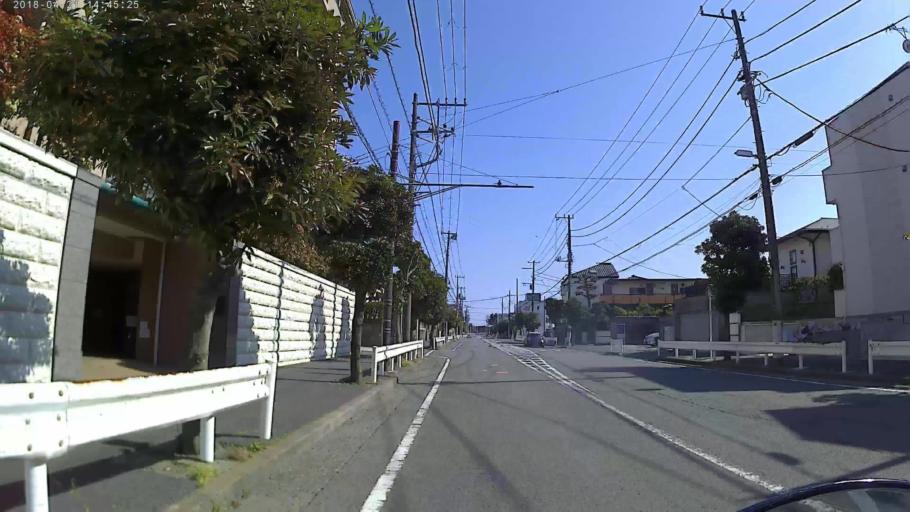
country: JP
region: Kanagawa
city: Hiratsuka
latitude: 35.3195
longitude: 139.3474
